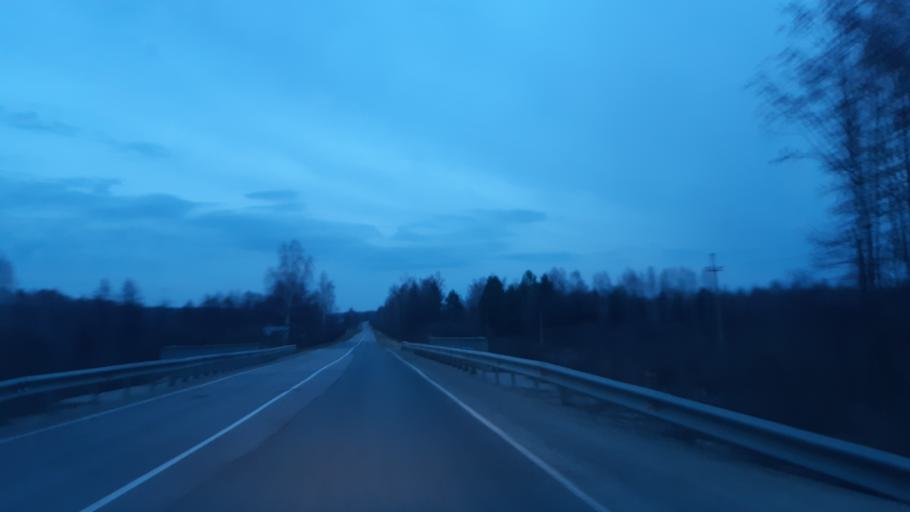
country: RU
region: Vladimir
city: Luknovo
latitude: 56.1784
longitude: 42.0086
